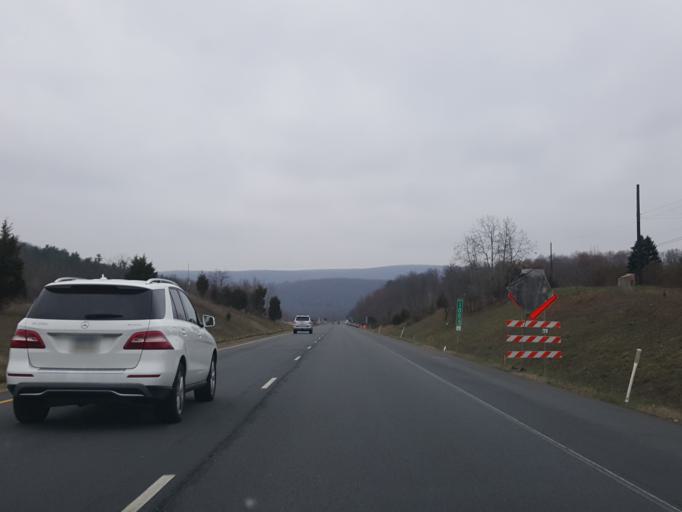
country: US
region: Pennsylvania
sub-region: Schuylkill County
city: Pine Grove
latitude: 40.5472
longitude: -76.4305
